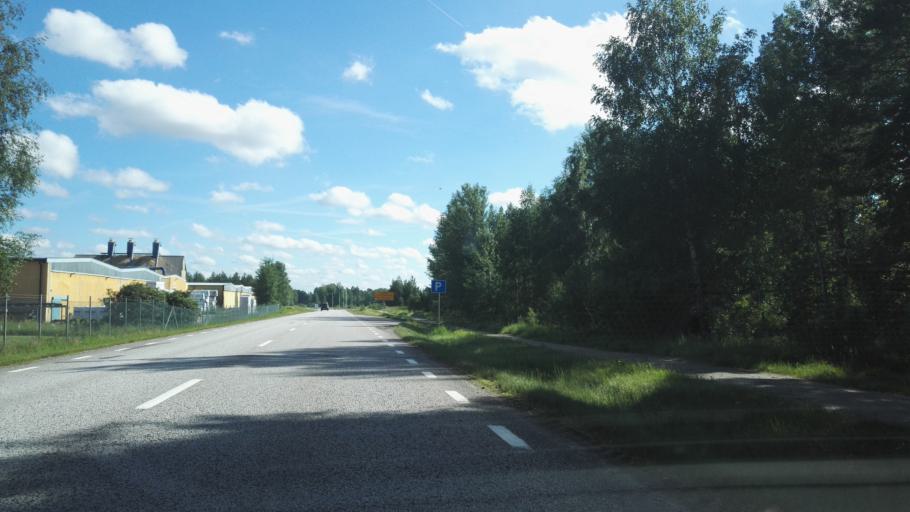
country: SE
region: Joenkoeping
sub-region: Savsjo Kommun
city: Vrigstad
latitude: 57.3473
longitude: 14.4728
